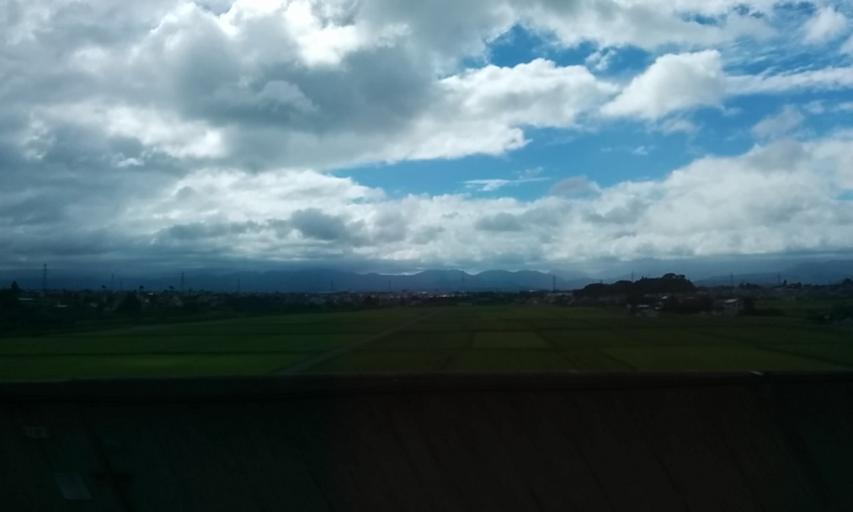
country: JP
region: Fukushima
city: Koriyama
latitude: 37.4402
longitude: 140.4022
